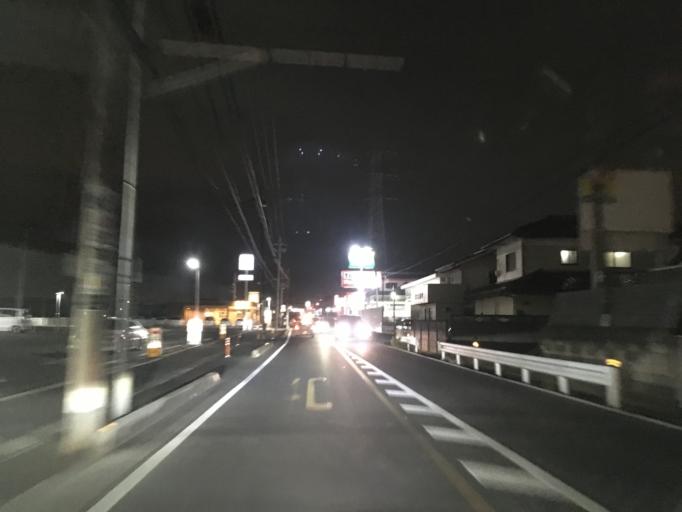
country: JP
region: Saitama
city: Sayama
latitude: 35.8310
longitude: 139.4321
